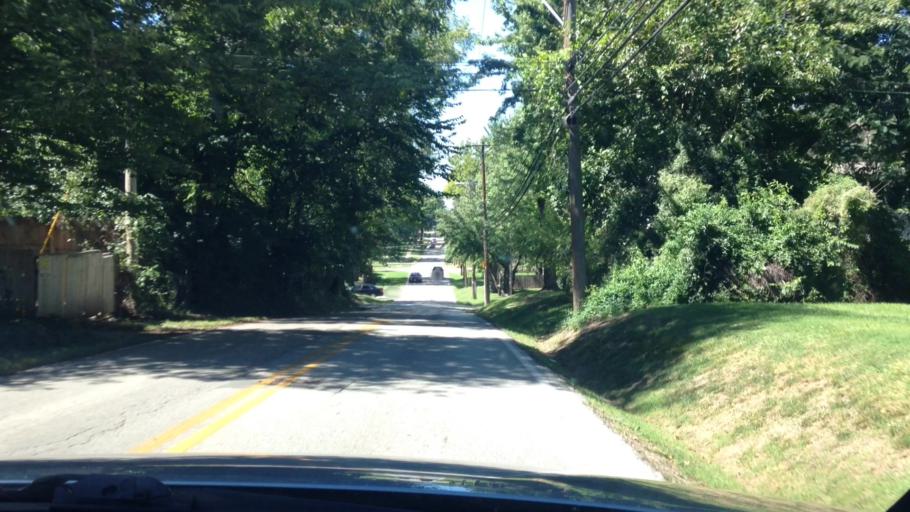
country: US
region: Kansas
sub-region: Johnson County
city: Leawood
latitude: 38.9667
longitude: -94.5885
